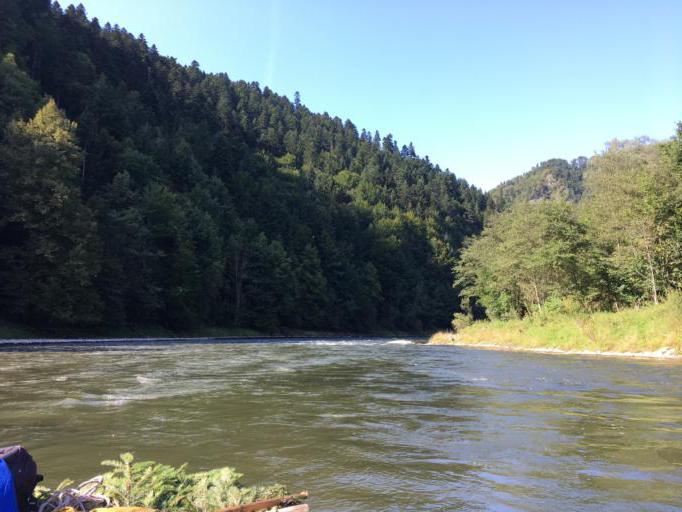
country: PL
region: Lesser Poland Voivodeship
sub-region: Powiat nowotarski
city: Kroscienko nad Dunajcem
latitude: 49.4004
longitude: 20.4346
